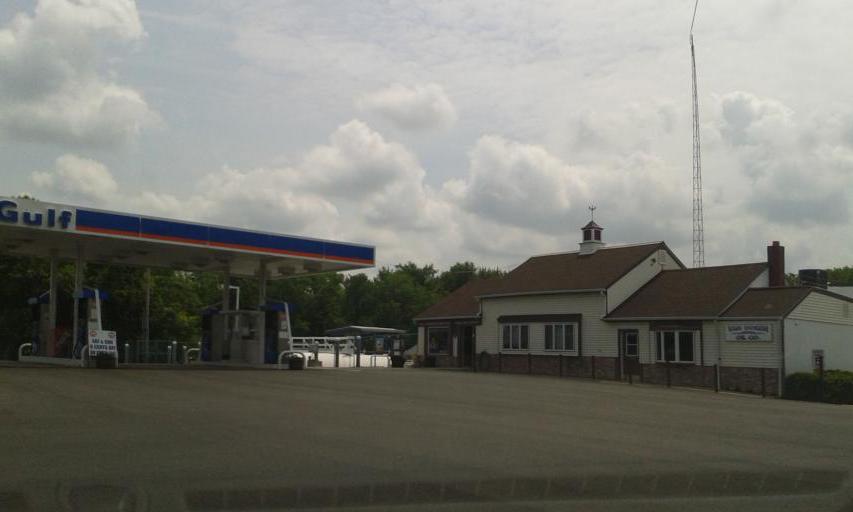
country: US
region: New Jersey
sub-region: Hunterdon County
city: Whitehouse Station
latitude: 40.6285
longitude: -74.7761
